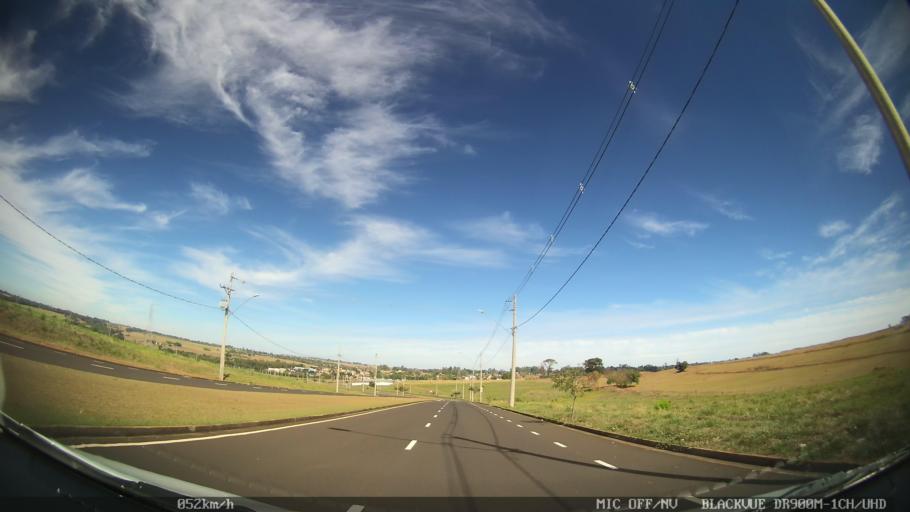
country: BR
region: Sao Paulo
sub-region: Sao Jose Do Rio Preto
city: Sao Jose do Rio Preto
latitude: -20.8528
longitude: -49.3793
